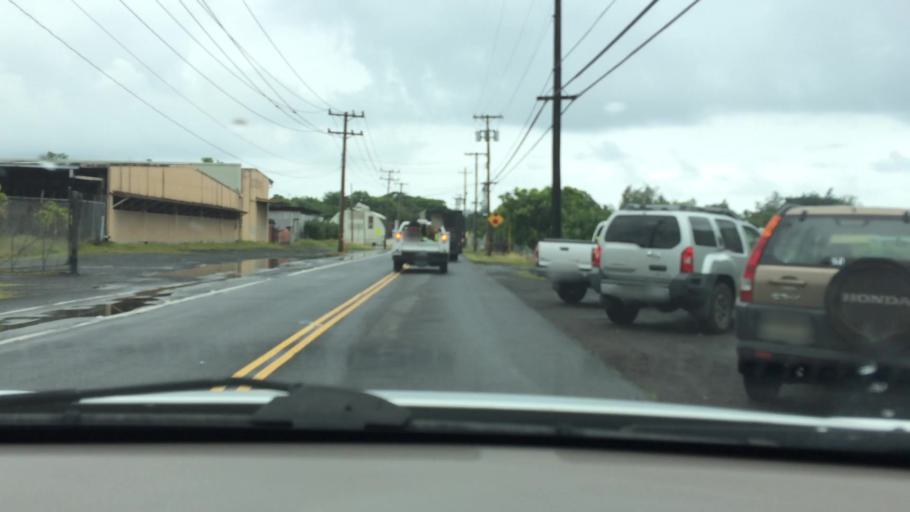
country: US
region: Hawaii
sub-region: Hawaii County
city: Hilo
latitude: 19.7199
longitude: -155.0657
